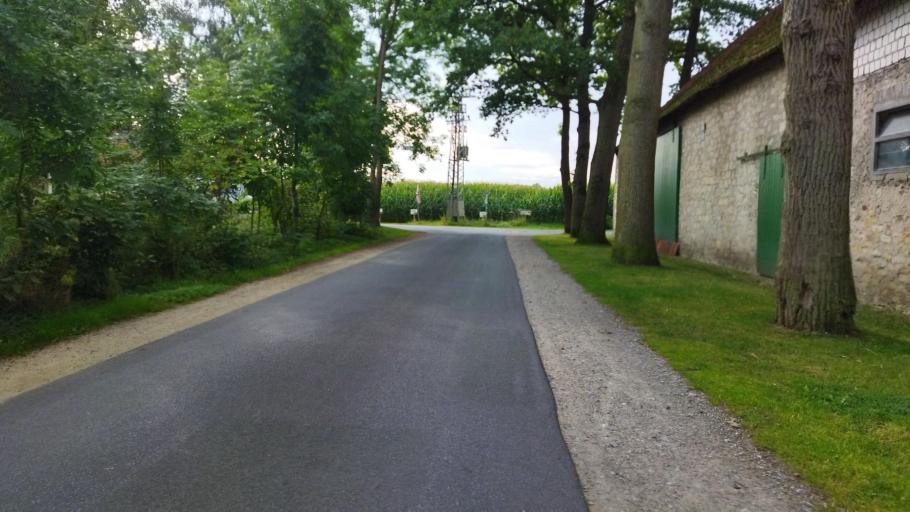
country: DE
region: Lower Saxony
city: Bad Laer
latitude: 52.0817
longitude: 8.1142
